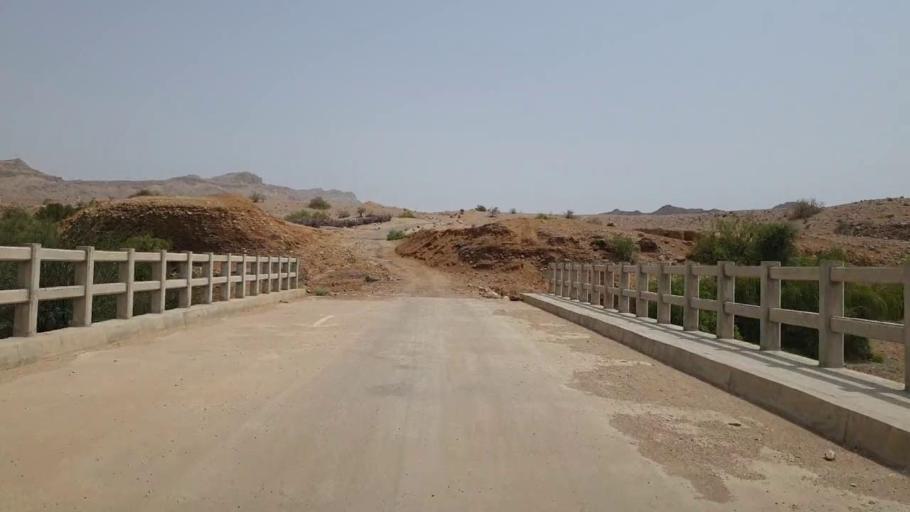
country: PK
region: Sindh
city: Sann
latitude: 25.8895
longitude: 67.9043
